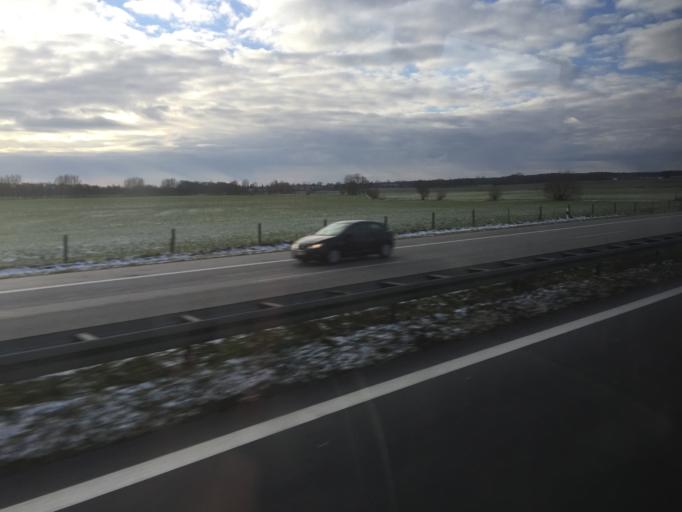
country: DE
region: Mecklenburg-Vorpommern
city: Locknitz
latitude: 53.3453
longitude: 11.8229
